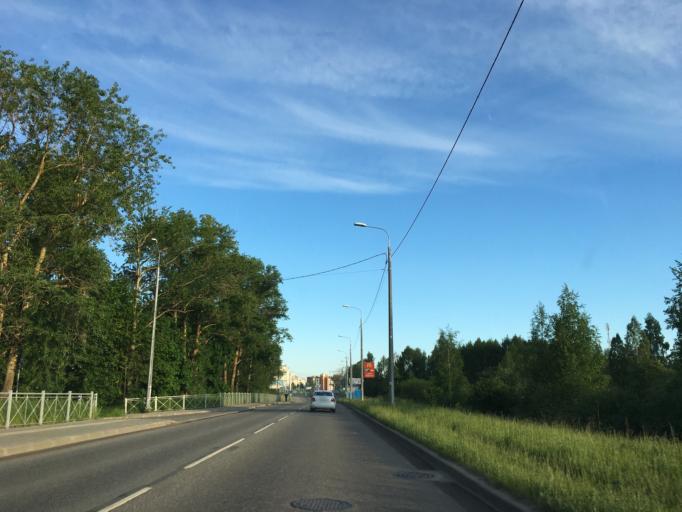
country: RU
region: Leningrad
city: Gatchina
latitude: 59.5877
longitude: 30.1357
